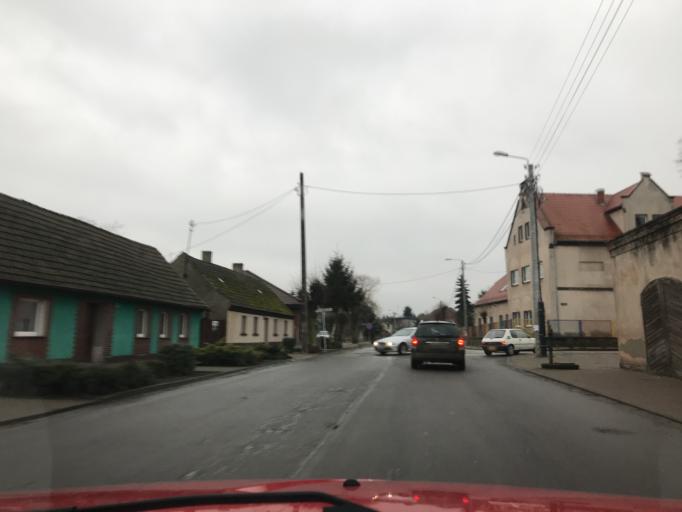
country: PL
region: Greater Poland Voivodeship
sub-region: Powiat ostrowski
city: Raszkow
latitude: 51.7171
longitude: 17.7287
